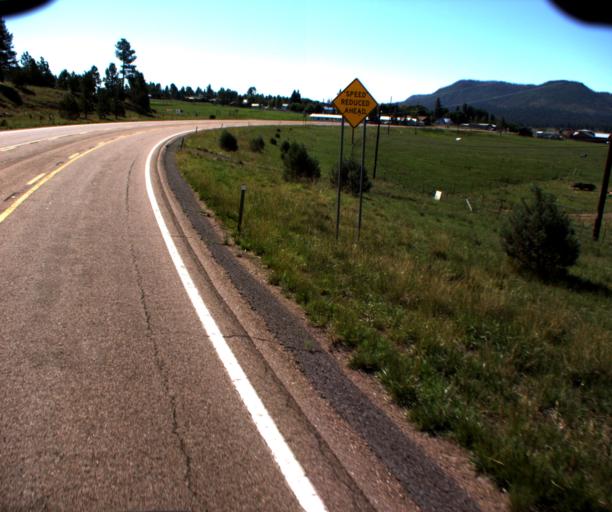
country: US
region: Arizona
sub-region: Apache County
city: Eagar
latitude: 33.8528
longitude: -109.1479
